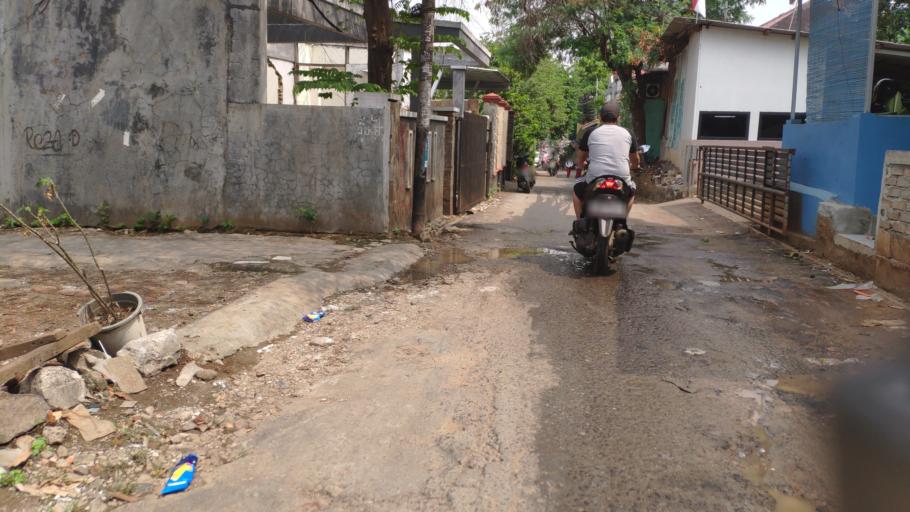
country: ID
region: West Java
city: Depok
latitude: -6.3225
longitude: 106.8276
